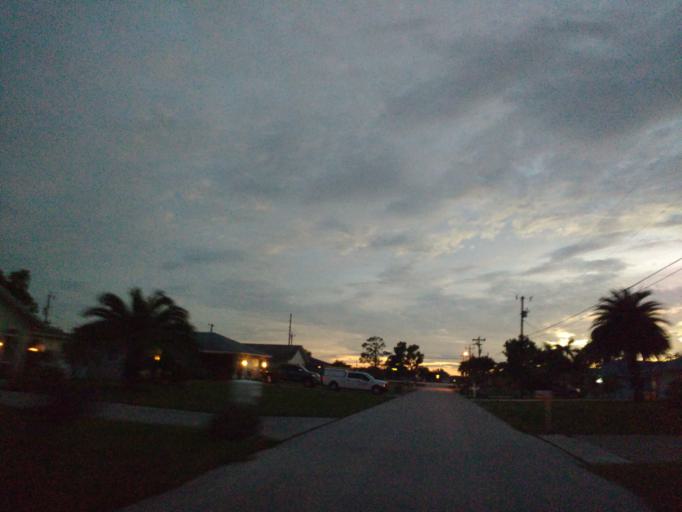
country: US
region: Florida
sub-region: Lee County
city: Cape Coral
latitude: 26.6209
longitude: -81.9721
